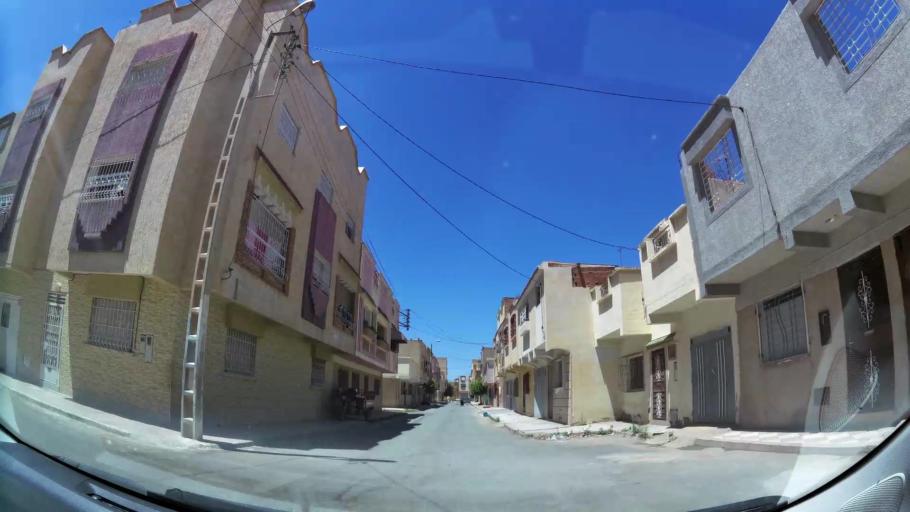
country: MA
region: Oriental
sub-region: Oujda-Angad
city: Oujda
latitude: 34.6822
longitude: -1.8739
